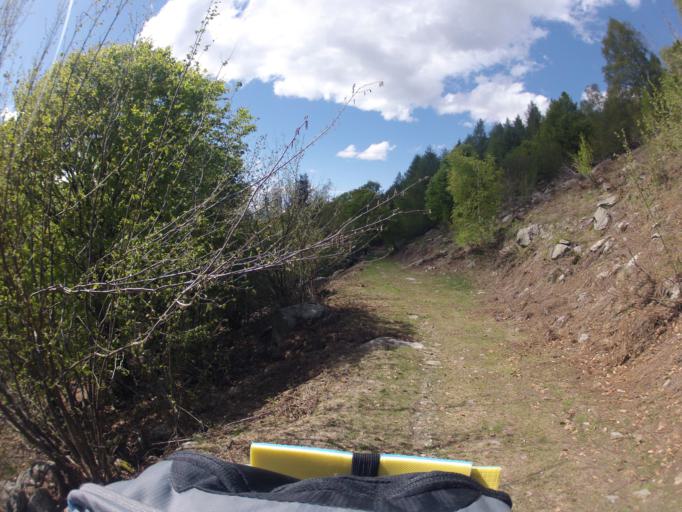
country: IT
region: Piedmont
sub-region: Provincia di Cuneo
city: Peveragno
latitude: 44.2758
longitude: 7.5847
